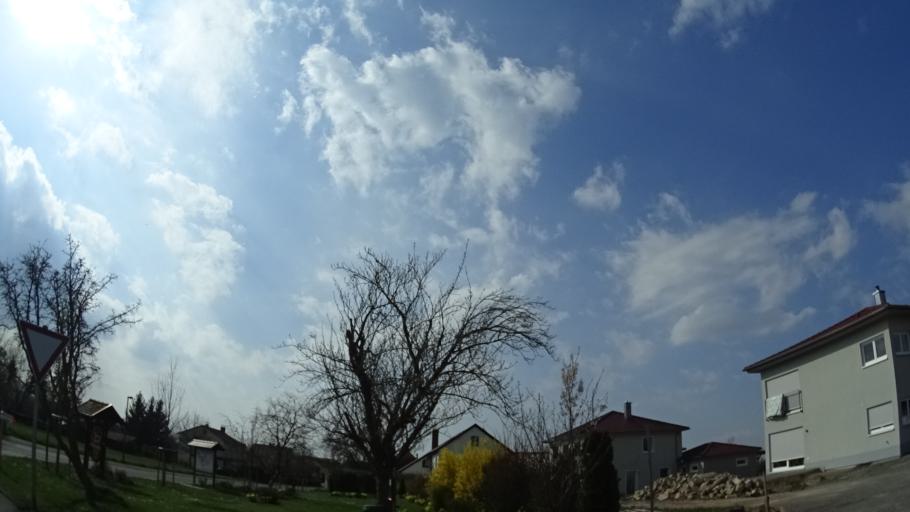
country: DE
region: Bavaria
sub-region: Regierungsbezirk Unterfranken
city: Castell
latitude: 49.7711
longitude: 10.3790
